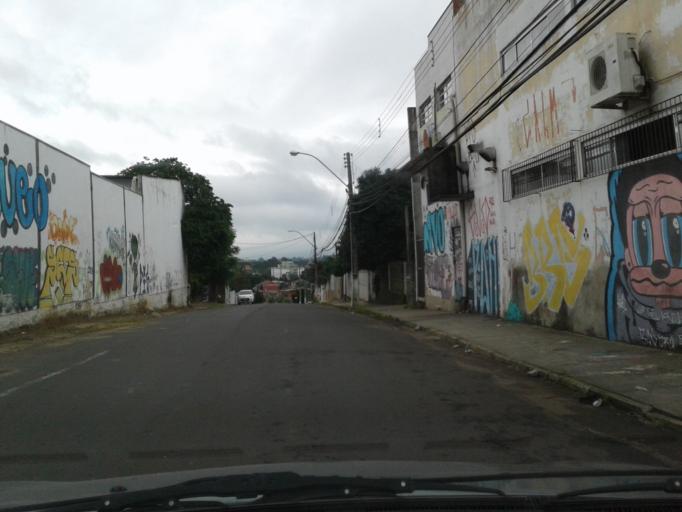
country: BR
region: Rio Grande do Sul
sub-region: Gravatai
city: Gravatai
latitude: -29.9349
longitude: -51.0153
